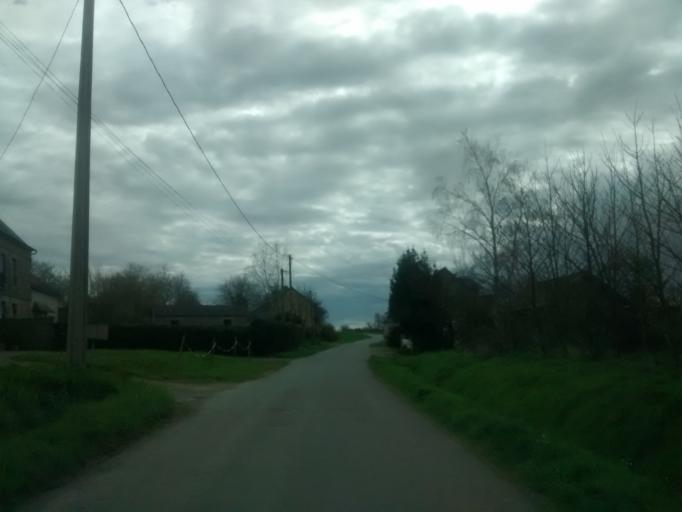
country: FR
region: Brittany
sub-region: Departement d'Ille-et-Vilaine
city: Erce-pres-Liffre
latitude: 48.2460
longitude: -1.5321
